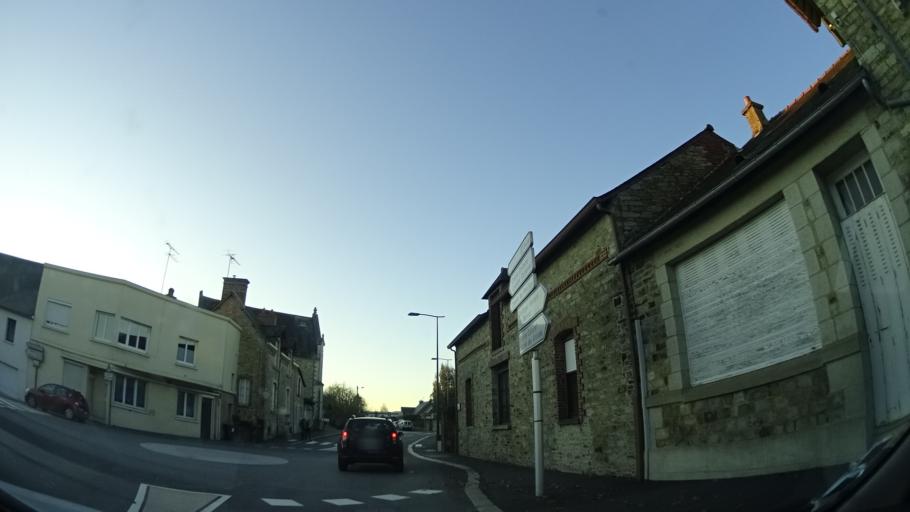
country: FR
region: Brittany
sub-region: Departement d'Ille-et-Vilaine
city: Vitre
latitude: 48.1201
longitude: -1.2162
